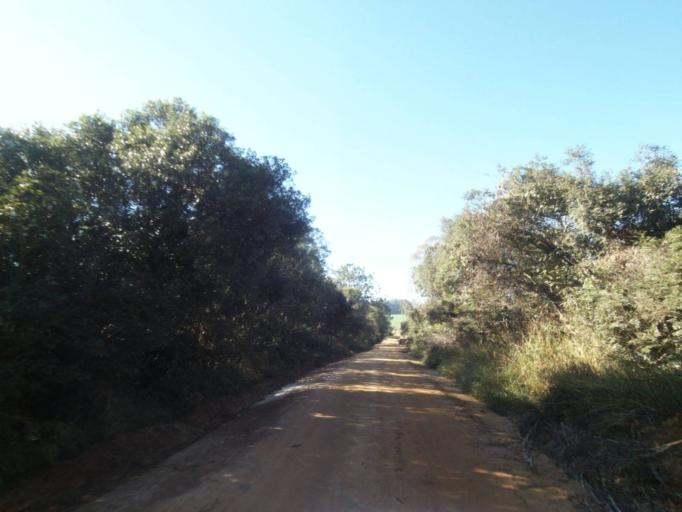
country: BR
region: Parana
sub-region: Tibagi
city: Tibagi
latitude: -24.5359
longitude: -50.3718
